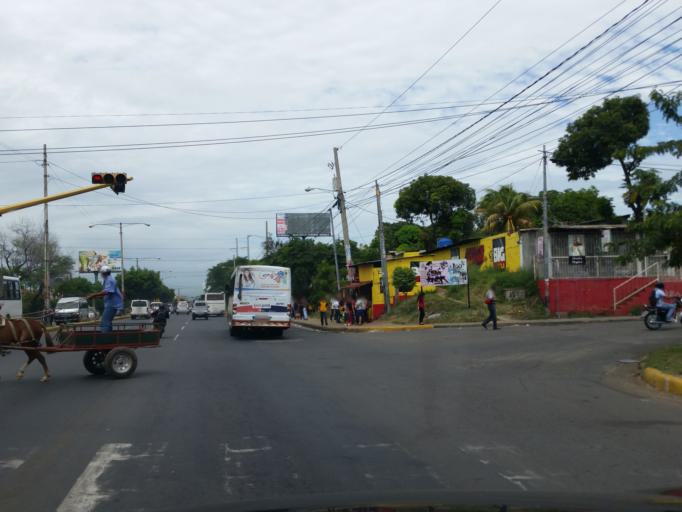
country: NI
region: Managua
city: Managua
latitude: 12.1485
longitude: -86.1995
